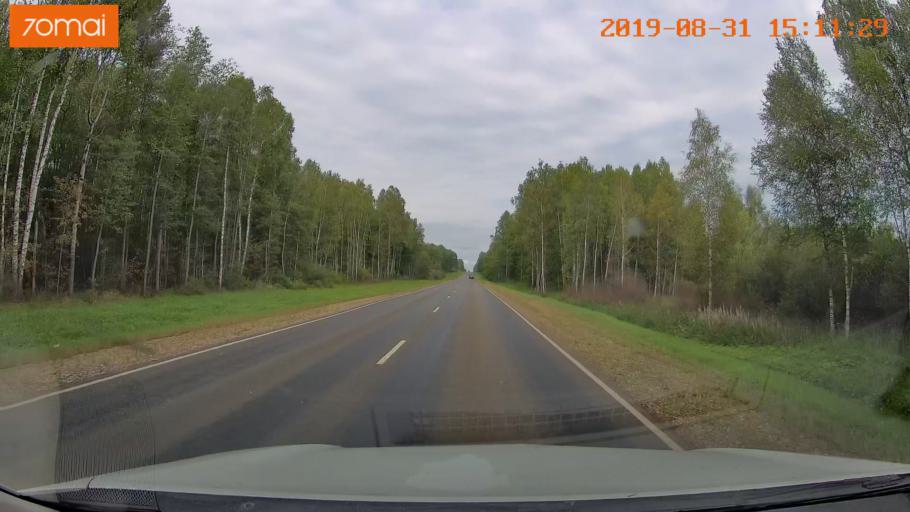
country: RU
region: Kaluga
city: Spas-Demensk
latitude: 54.4229
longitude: 34.2448
